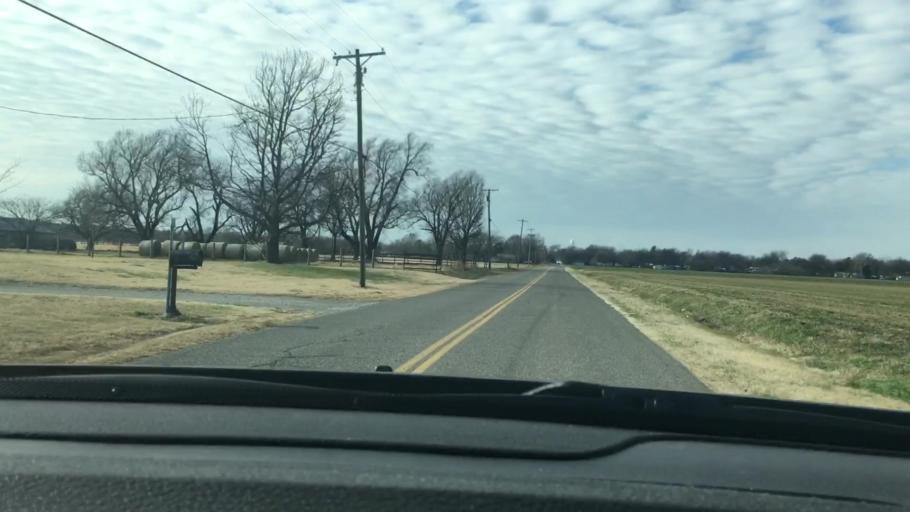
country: US
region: Oklahoma
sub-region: Garvin County
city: Pauls Valley
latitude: 34.7388
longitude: -97.1990
